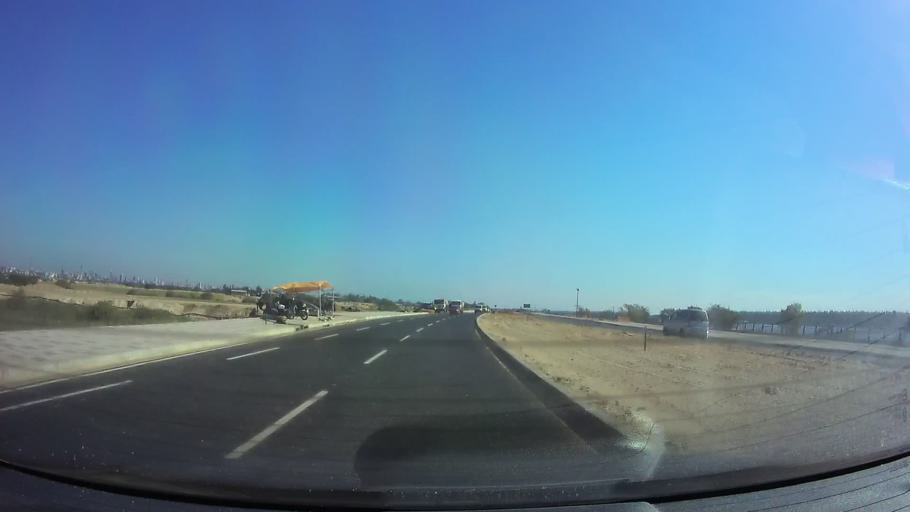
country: PY
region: Asuncion
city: Asuncion
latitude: -25.2460
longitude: -57.5938
